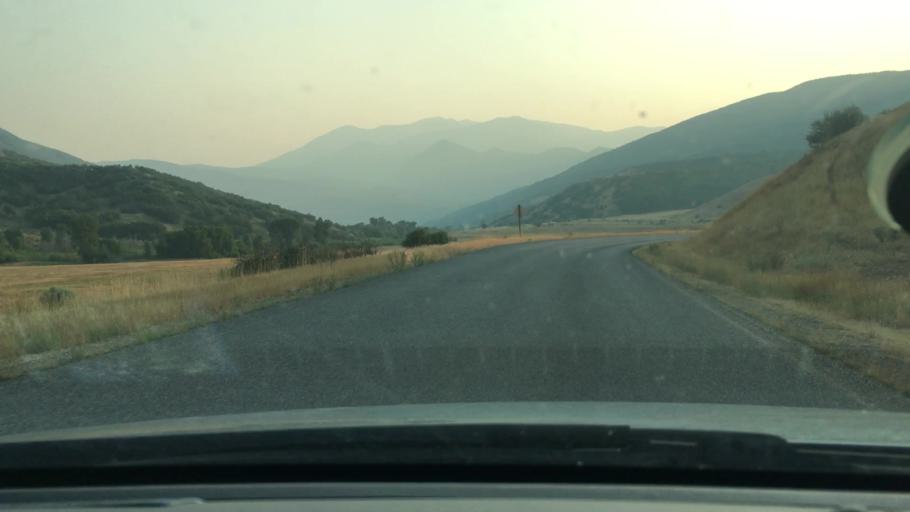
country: US
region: Utah
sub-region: Utah County
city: Mapleton
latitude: 40.0474
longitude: -111.4697
